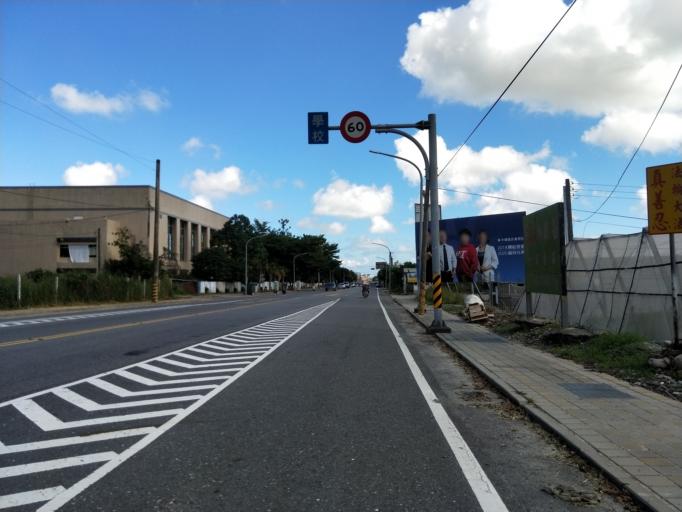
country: TW
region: Taiwan
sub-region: Taitung
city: Taitung
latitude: 22.7893
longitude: 121.1105
